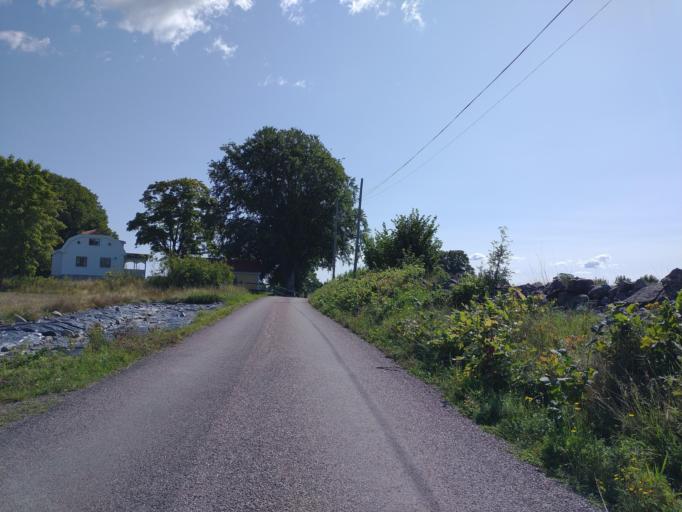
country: SE
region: Kalmar
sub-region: Kalmar Kommun
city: Lindsdal
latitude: 56.7930
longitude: 16.2884
